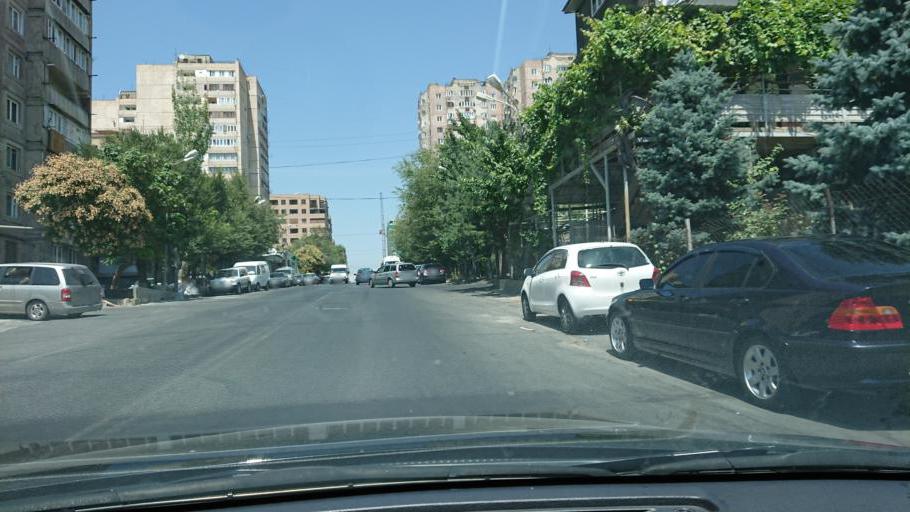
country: AM
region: Yerevan
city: Yerevan
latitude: 40.1971
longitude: 44.5027
